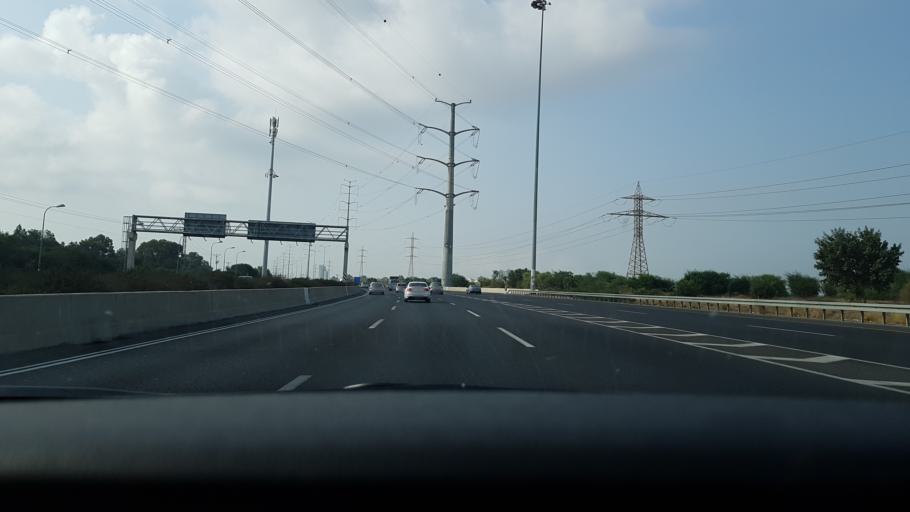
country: IL
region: Central District
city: Bet Dagan
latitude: 31.9971
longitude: 34.8010
